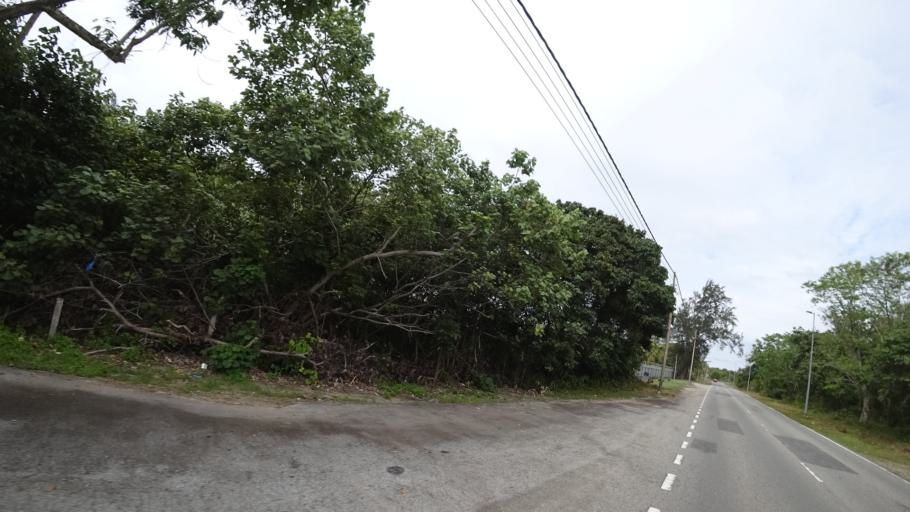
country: BN
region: Tutong
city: Tutong
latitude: 4.8068
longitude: 114.6382
